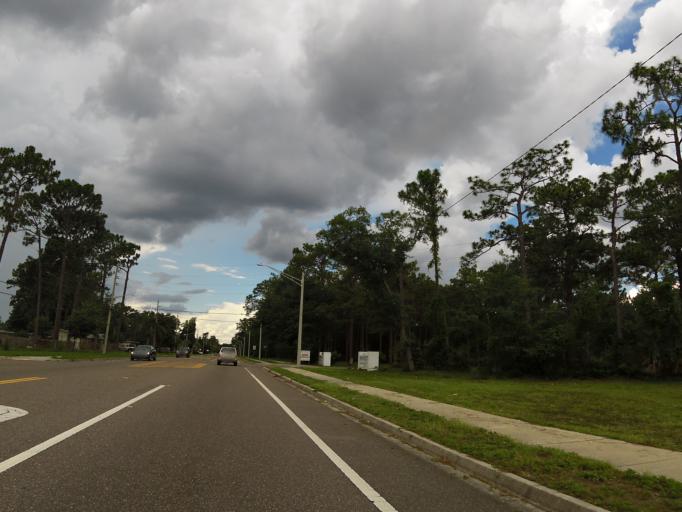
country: US
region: Florida
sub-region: Duval County
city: Jacksonville
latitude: 30.4167
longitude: -81.6654
